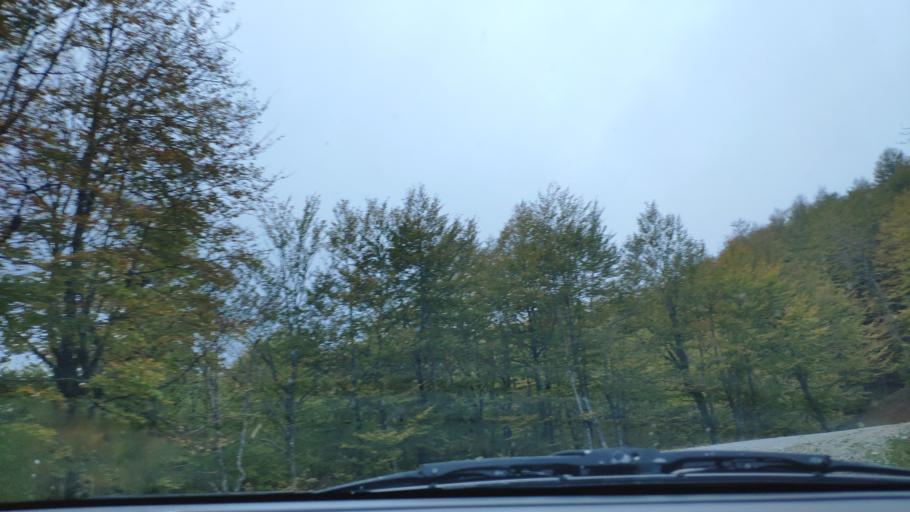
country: GR
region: West Macedonia
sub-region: Nomos Kastorias
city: Nestorio
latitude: 40.2987
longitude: 20.9076
